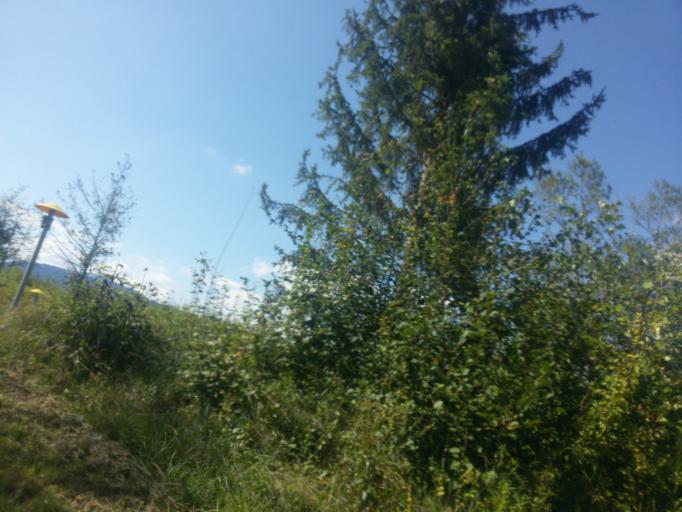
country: AT
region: Carinthia
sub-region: Politischer Bezirk Villach Land
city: Wernberg
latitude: 46.6082
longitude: 13.9019
